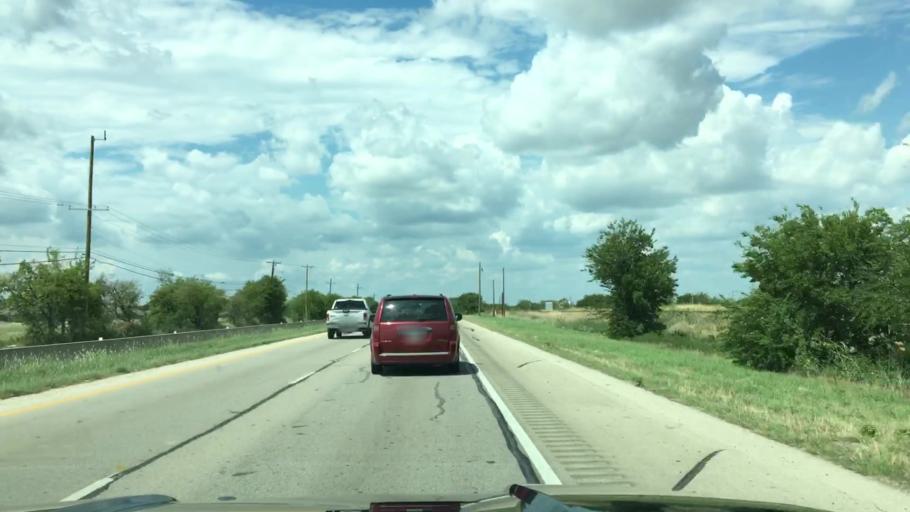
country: US
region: Texas
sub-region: Tarrant County
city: Saginaw
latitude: 32.8873
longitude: -97.3873
